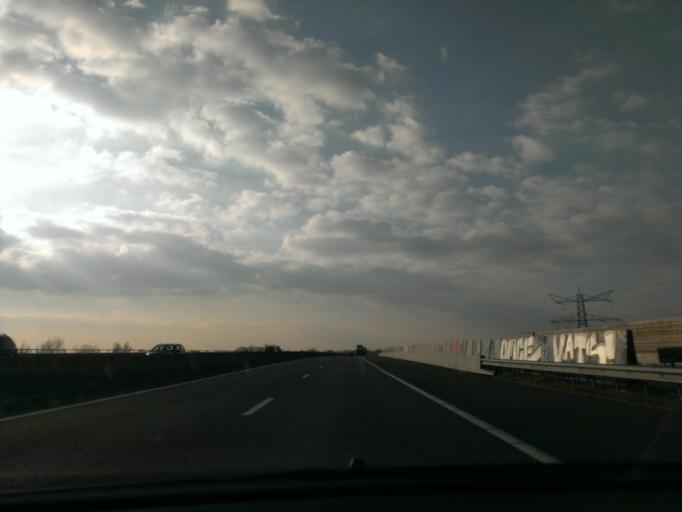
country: NL
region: Overijssel
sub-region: Gemeente Almelo
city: Almelo
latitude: 52.3259
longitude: 6.6296
